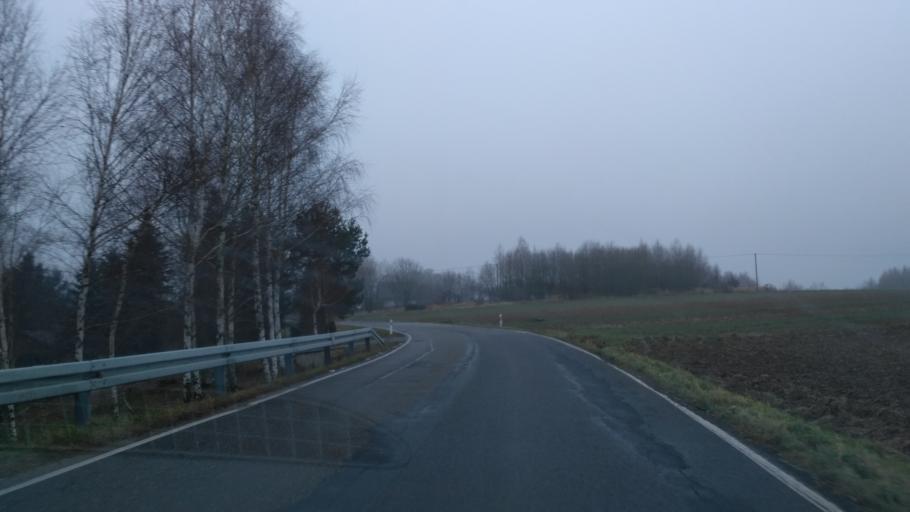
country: PL
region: Subcarpathian Voivodeship
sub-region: Powiat lancucki
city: Handzlowka
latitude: 49.9660
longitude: 22.1915
